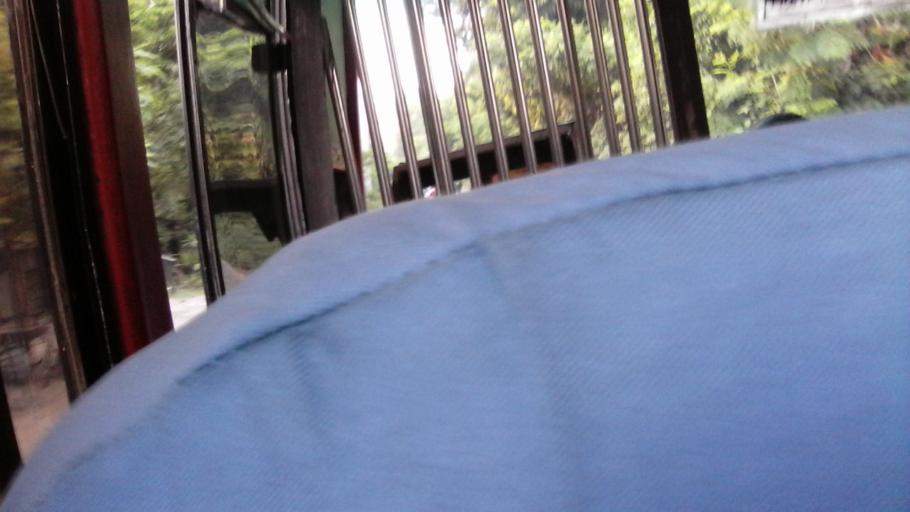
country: IN
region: West Bengal
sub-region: North 24 Parganas
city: Taki
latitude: 22.5721
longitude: 89.0005
